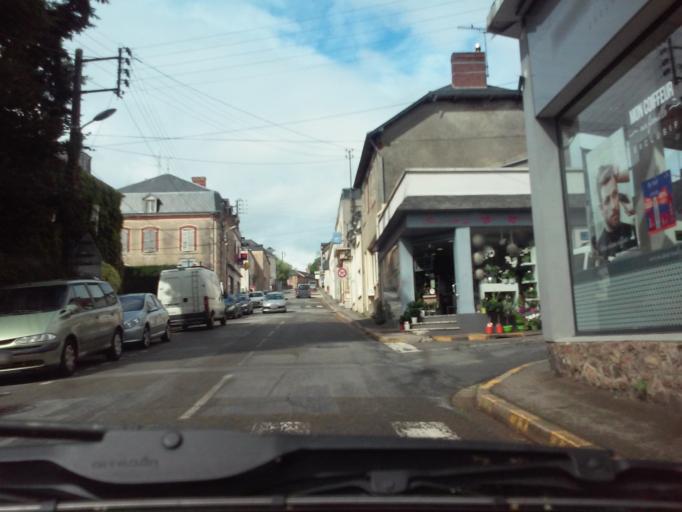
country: FR
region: Pays de la Loire
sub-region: Departement de la Mayenne
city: Port-Brillet
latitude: 48.1112
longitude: -0.9740
